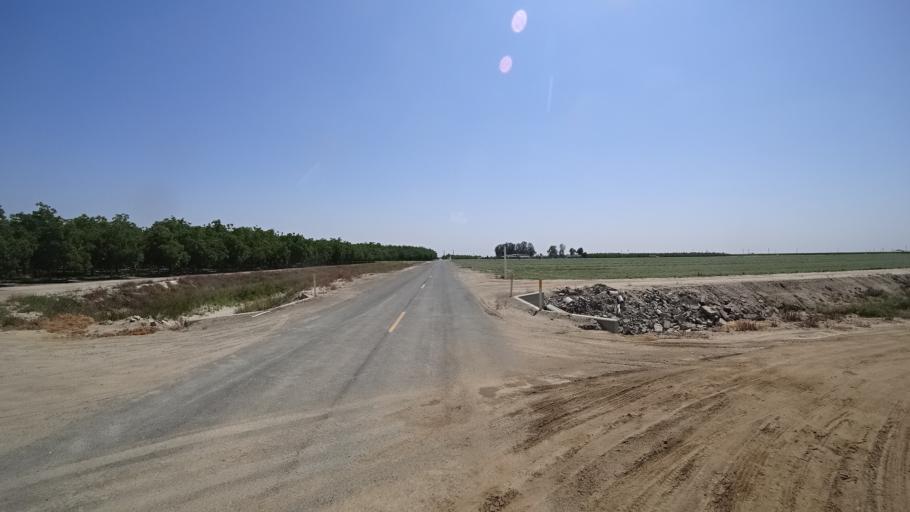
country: US
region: California
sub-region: Kings County
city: Home Garden
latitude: 36.2840
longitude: -119.5699
